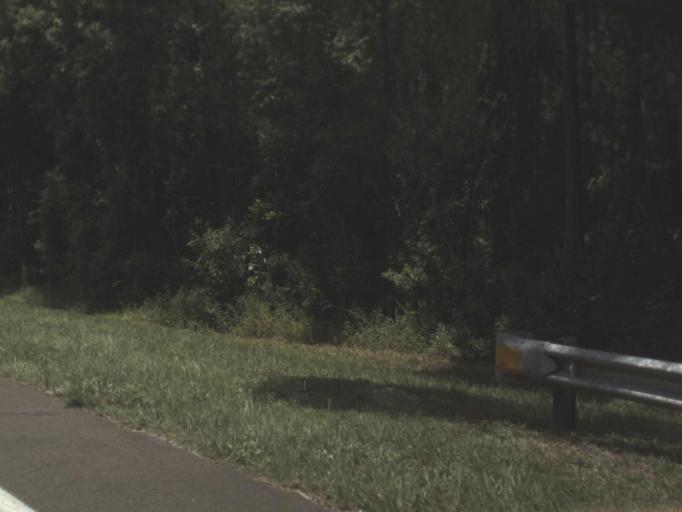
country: US
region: Florida
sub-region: Alachua County
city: Alachua
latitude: 29.7236
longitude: -82.3541
